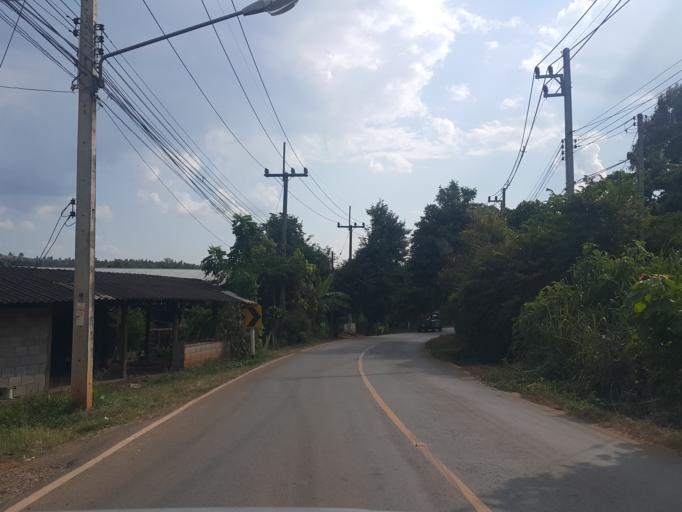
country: TH
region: Chiang Mai
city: Mae Chaem
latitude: 18.4869
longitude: 98.3829
